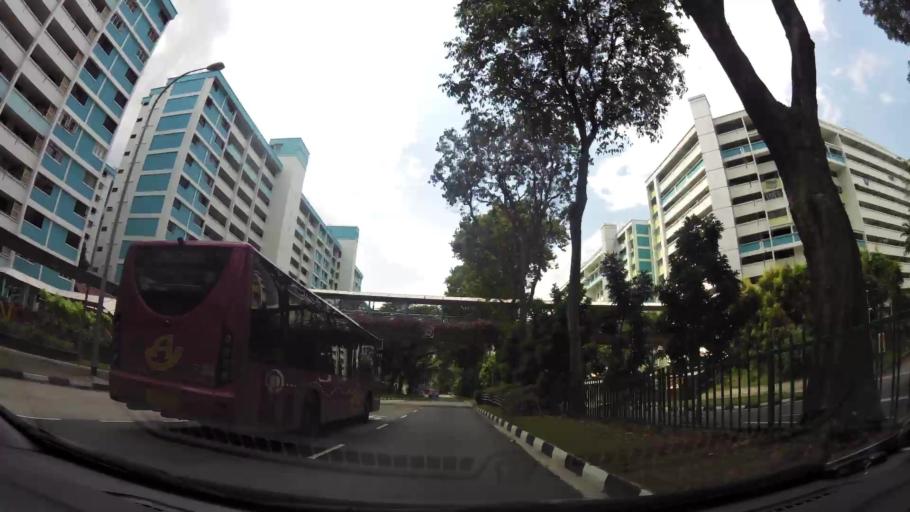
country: MY
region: Johor
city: Kampung Pasir Gudang Baru
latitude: 1.4305
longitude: 103.8328
